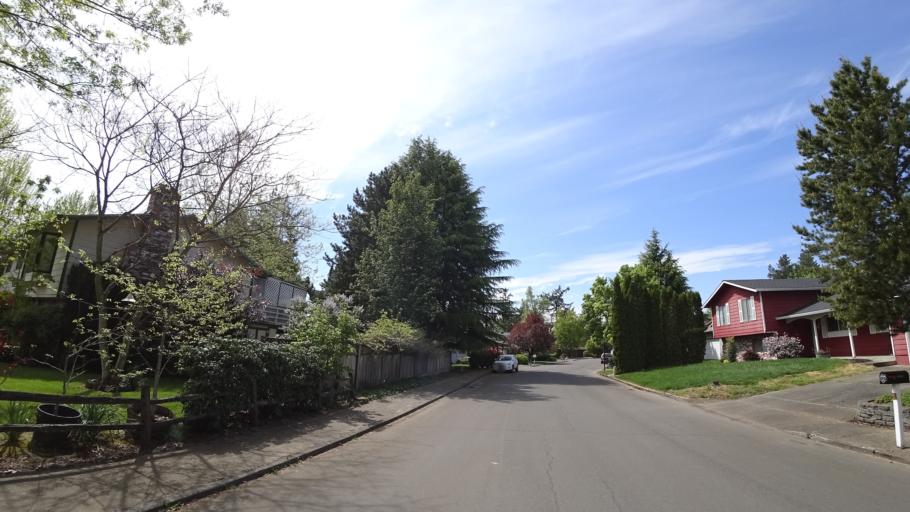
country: US
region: Oregon
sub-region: Washington County
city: Aloha
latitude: 45.4853
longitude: -122.8887
